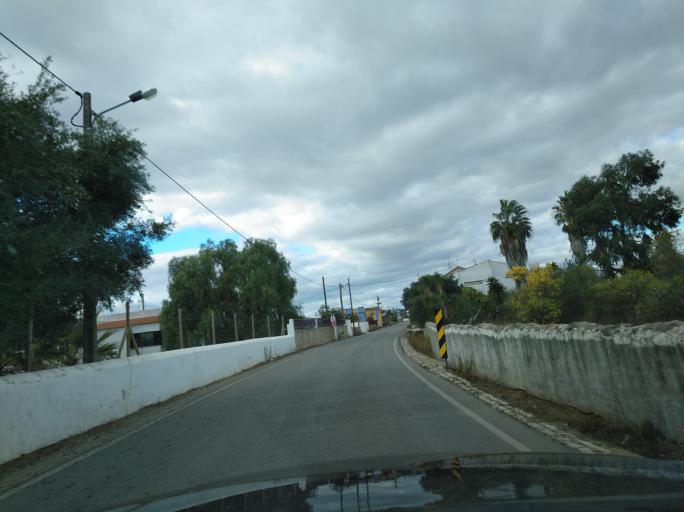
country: PT
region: Faro
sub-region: Tavira
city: Luz
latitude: 37.0983
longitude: -7.7067
